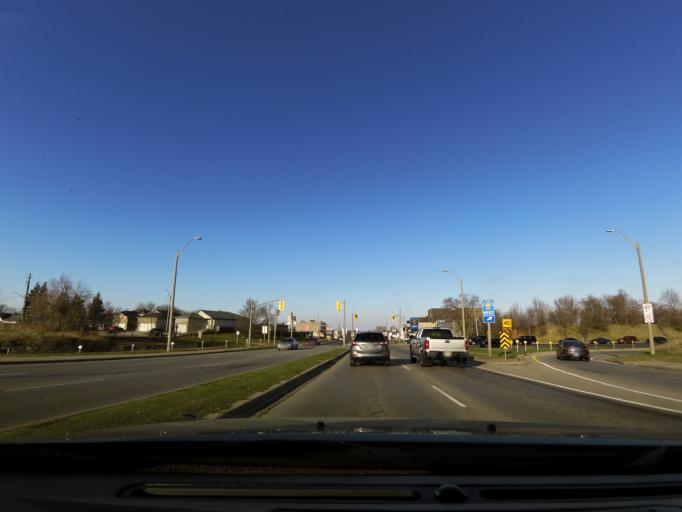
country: CA
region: Ontario
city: Hamilton
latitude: 43.2191
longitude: -79.8858
